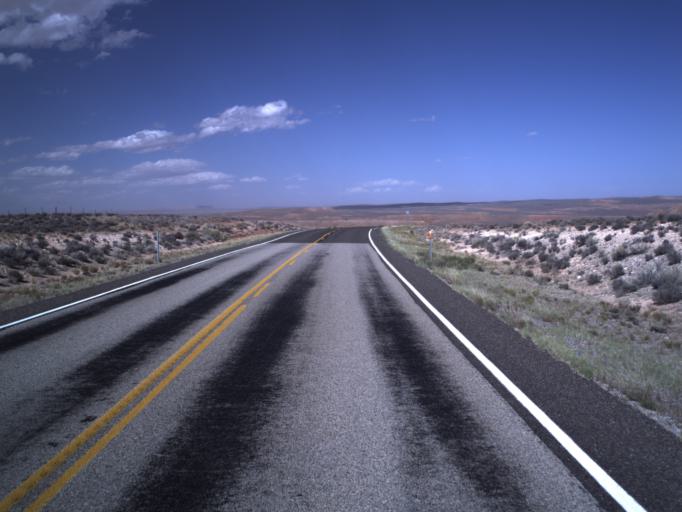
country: US
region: Utah
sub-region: Wayne County
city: Loa
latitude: 38.1201
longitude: -110.6216
